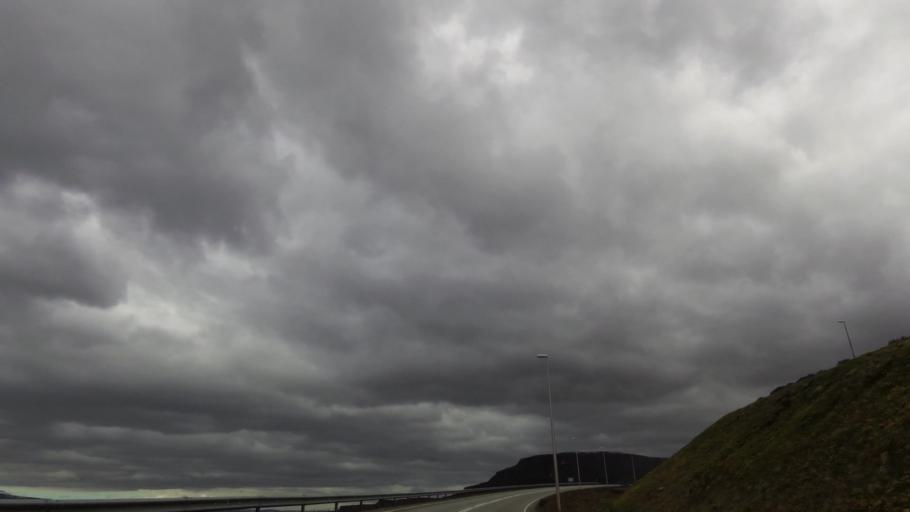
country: IS
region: Westfjords
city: Isafjoerdur
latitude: 66.1086
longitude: -23.1137
